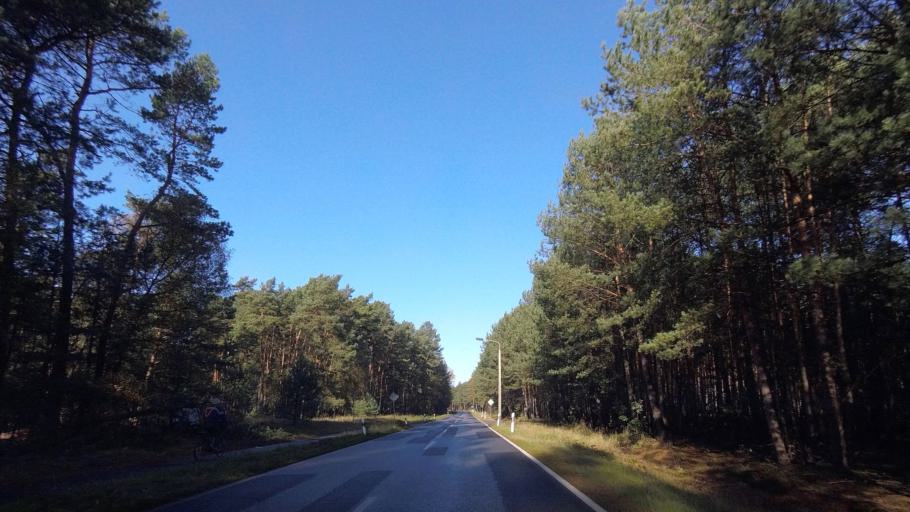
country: DE
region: Brandenburg
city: Borkwalde
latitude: 52.2480
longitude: 12.8466
